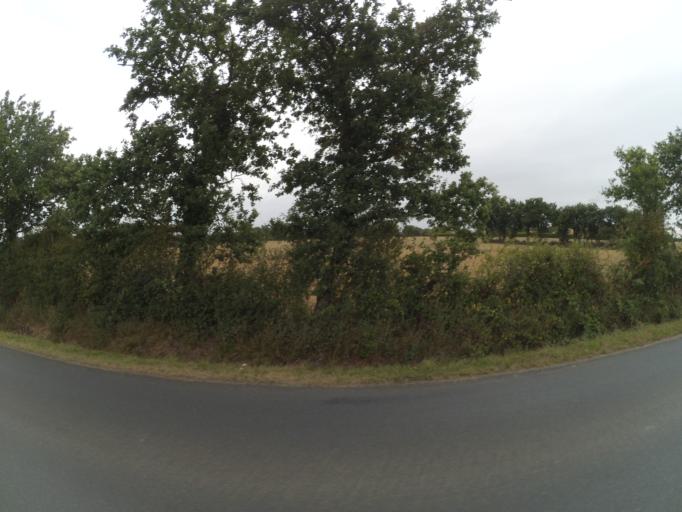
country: FR
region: Pays de la Loire
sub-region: Departement de la Vendee
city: Saint-Andre-Treize-Voies
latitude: 46.9444
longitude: -1.4129
